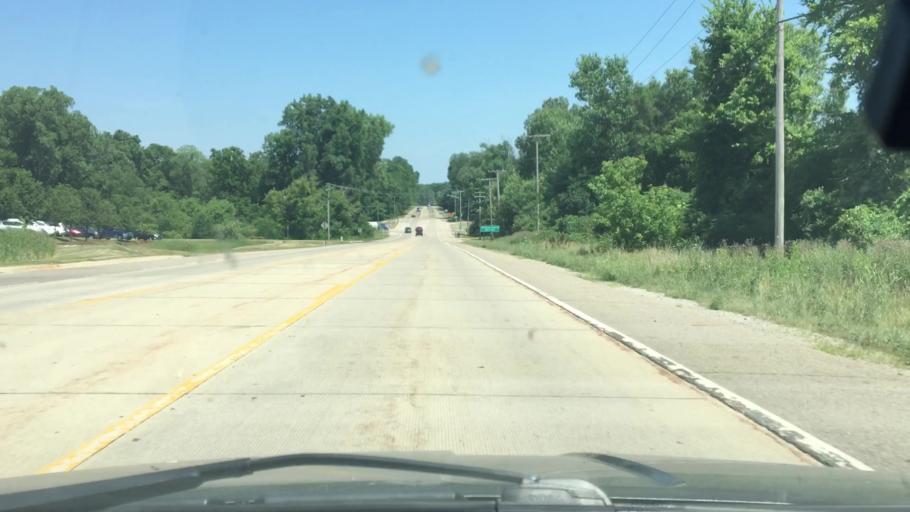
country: US
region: Michigan
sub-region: Livingston County
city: Brighton
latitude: 42.5158
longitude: -83.7239
